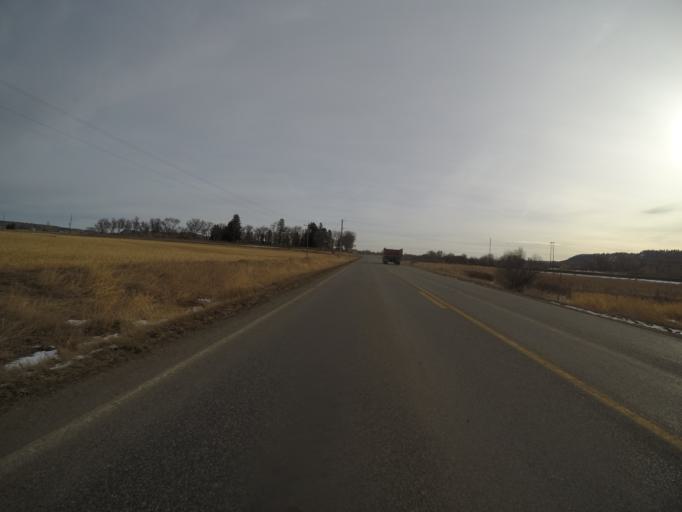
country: US
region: Montana
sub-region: Stillwater County
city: Columbus
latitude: 45.6416
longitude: -109.2768
